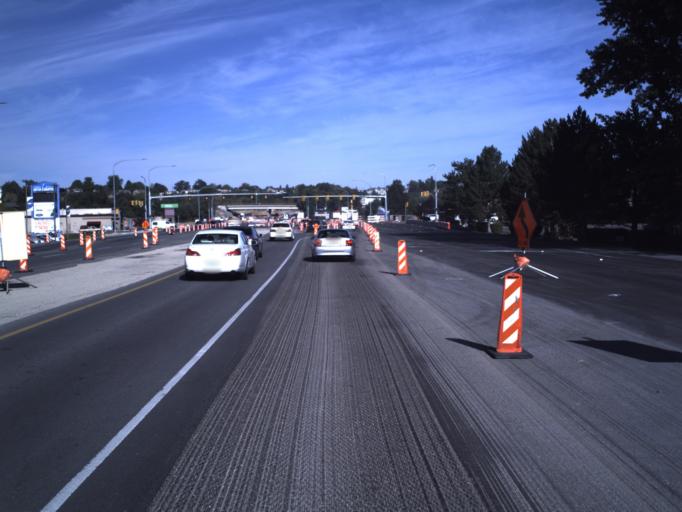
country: US
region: Utah
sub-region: Utah County
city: Provo
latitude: 40.2617
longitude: -111.6657
